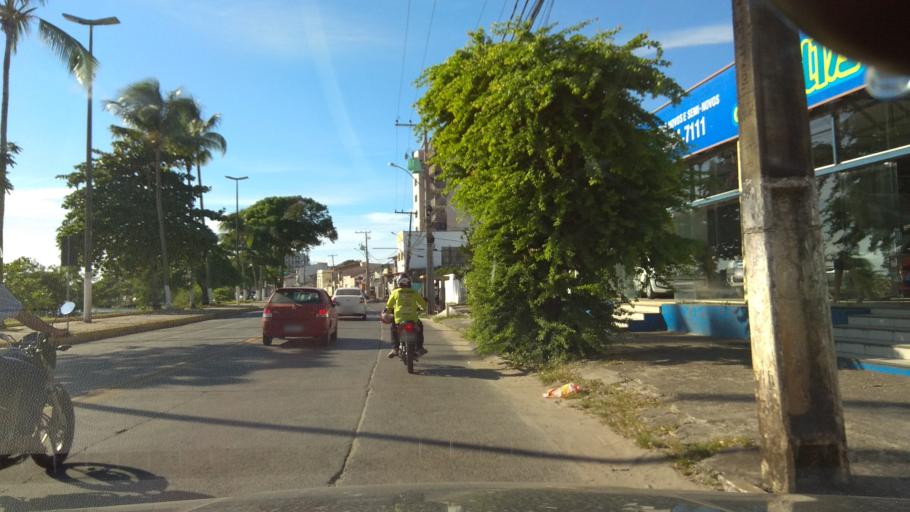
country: BR
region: Bahia
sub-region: Ilheus
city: Ilheus
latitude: -14.8112
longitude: -39.0333
